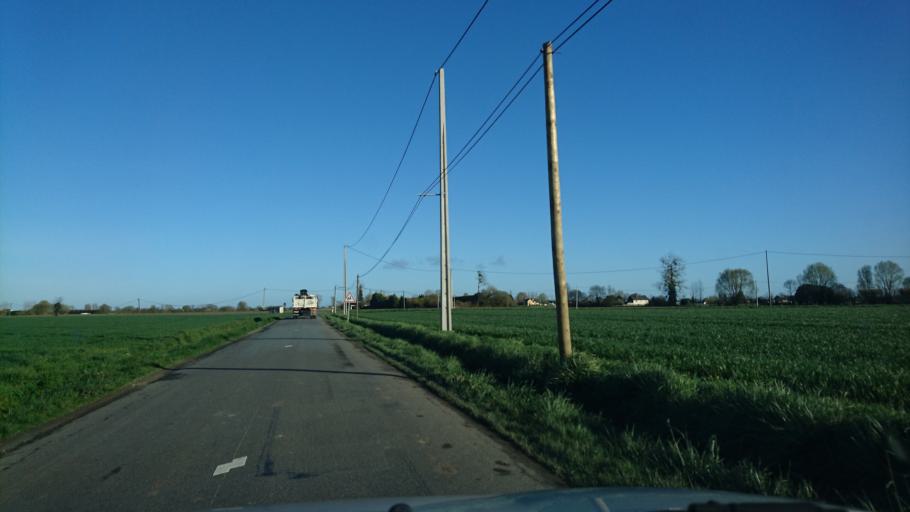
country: FR
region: Brittany
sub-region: Departement d'Ille-et-Vilaine
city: Cherrueix
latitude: 48.5856
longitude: -1.7174
